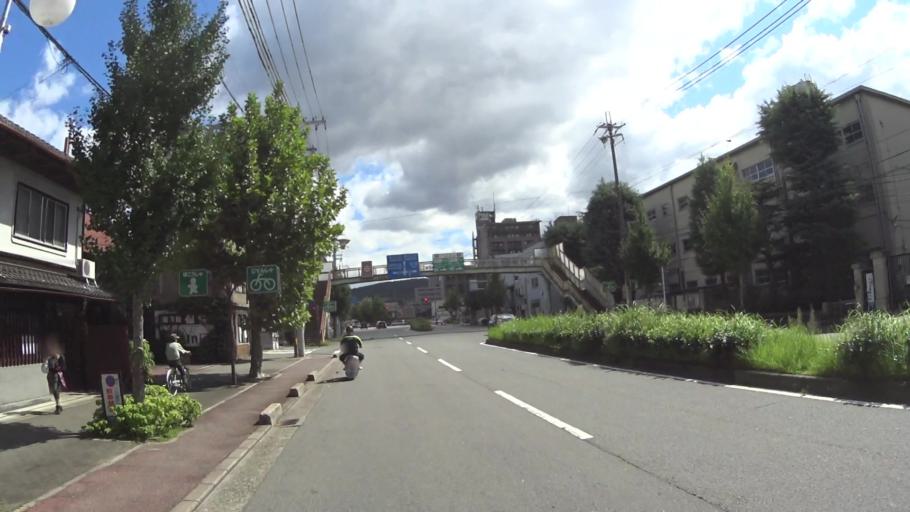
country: JP
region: Kyoto
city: Kyoto
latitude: 34.9797
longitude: 135.7623
